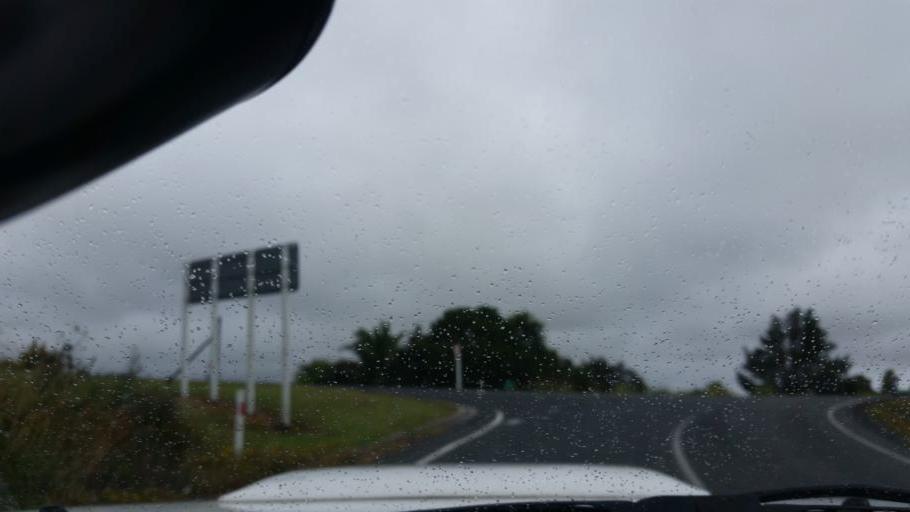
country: NZ
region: Auckland
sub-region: Auckland
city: Wellsford
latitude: -36.1325
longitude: 174.5291
